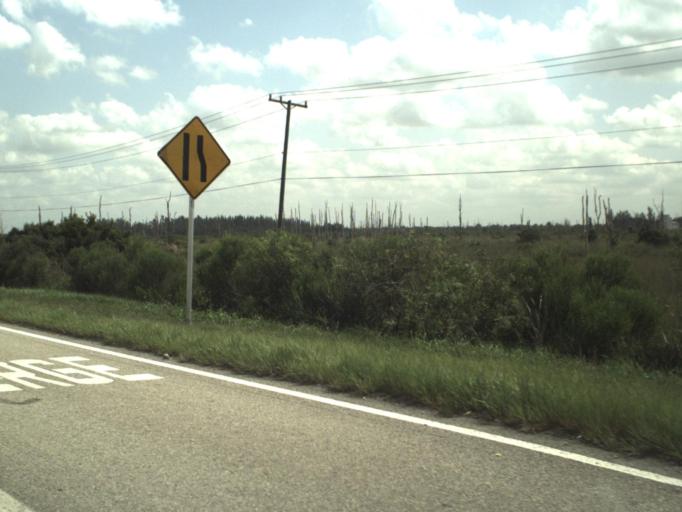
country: US
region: Florida
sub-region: Broward County
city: Weston
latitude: 25.9948
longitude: -80.4320
